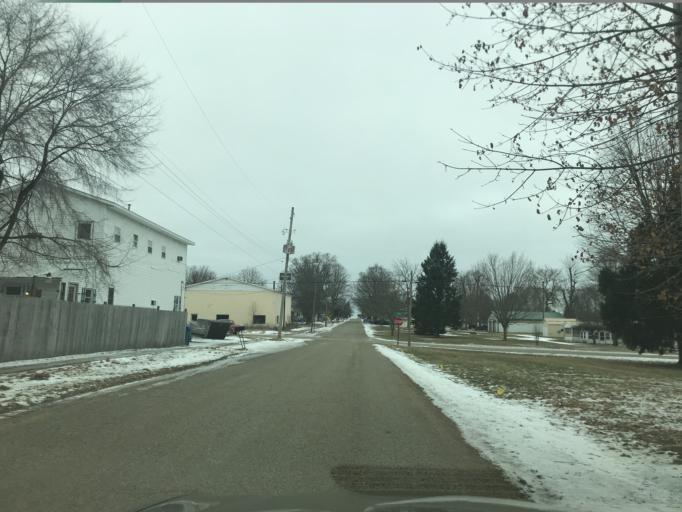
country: US
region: Michigan
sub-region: Jackson County
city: Brooklyn
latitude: 42.0693
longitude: -84.3305
